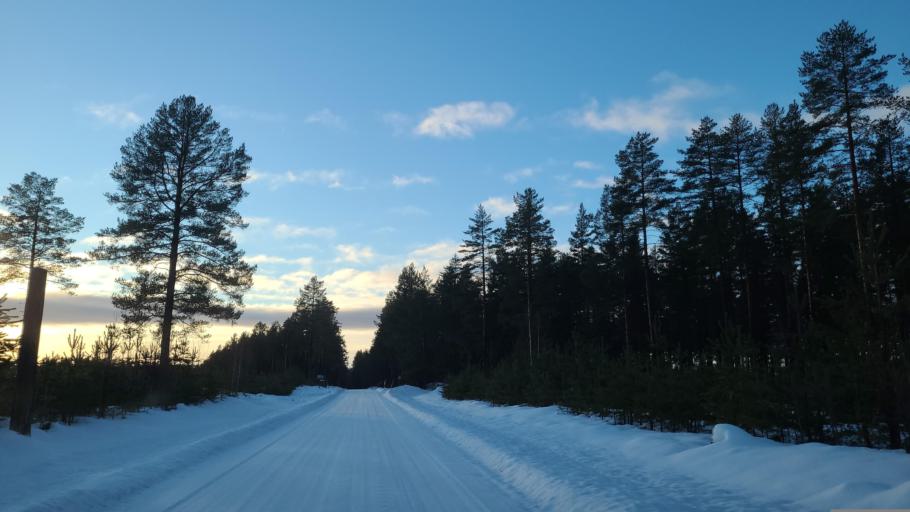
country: SE
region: Gaevleborg
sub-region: Bollnas Kommun
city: Kilafors
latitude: 61.3681
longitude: 16.6683
